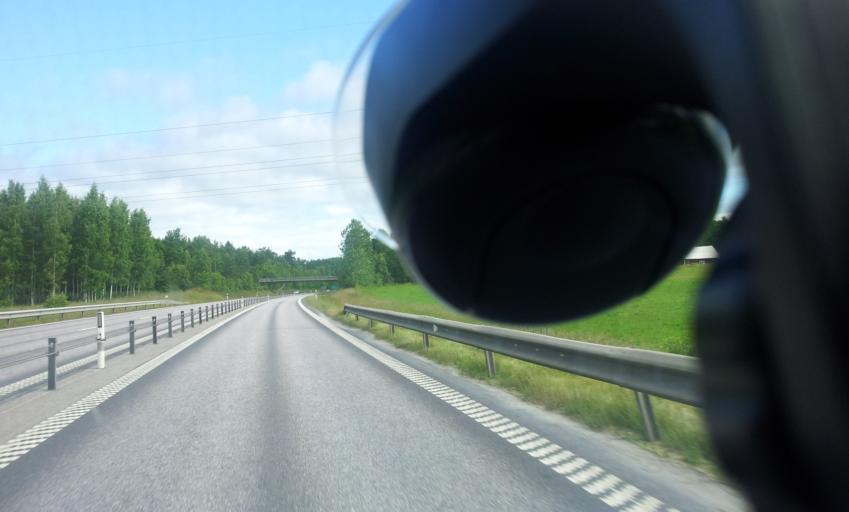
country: SE
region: Kalmar
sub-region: Kalmar Kommun
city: Lindsdal
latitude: 56.7462
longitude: 16.3055
